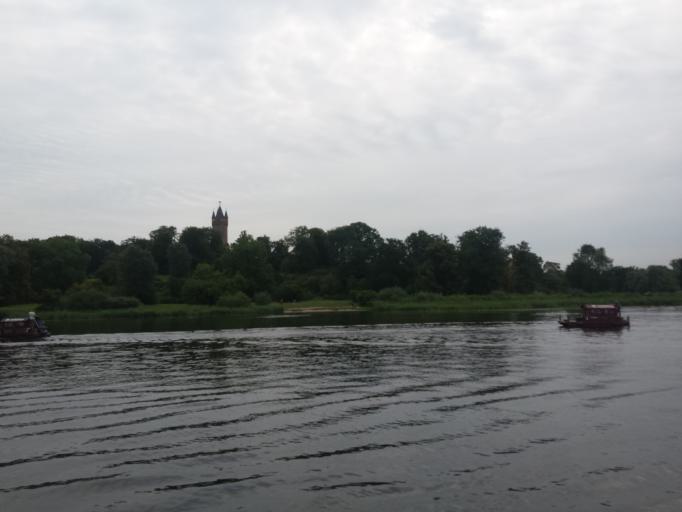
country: DE
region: Brandenburg
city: Potsdam
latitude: 52.4046
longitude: 13.0811
